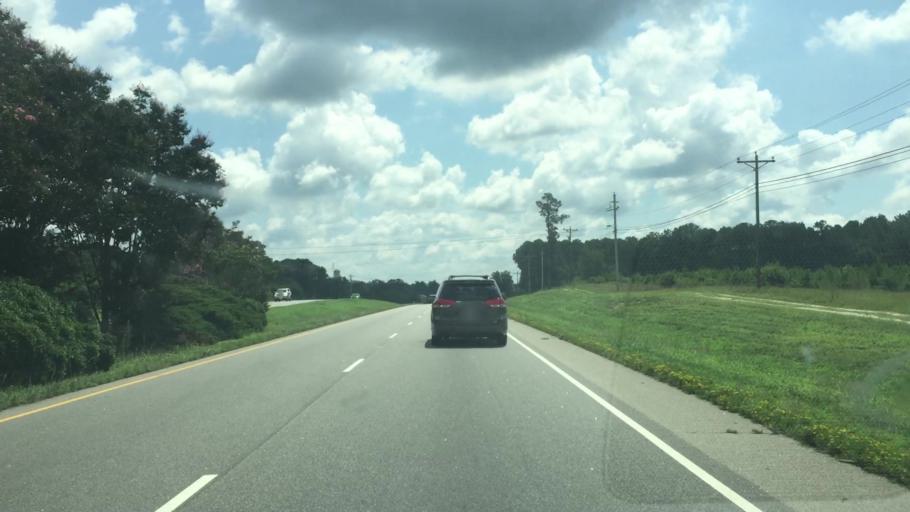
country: US
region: North Carolina
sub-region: Scotland County
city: Laurel Hill
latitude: 34.8117
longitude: -79.5582
